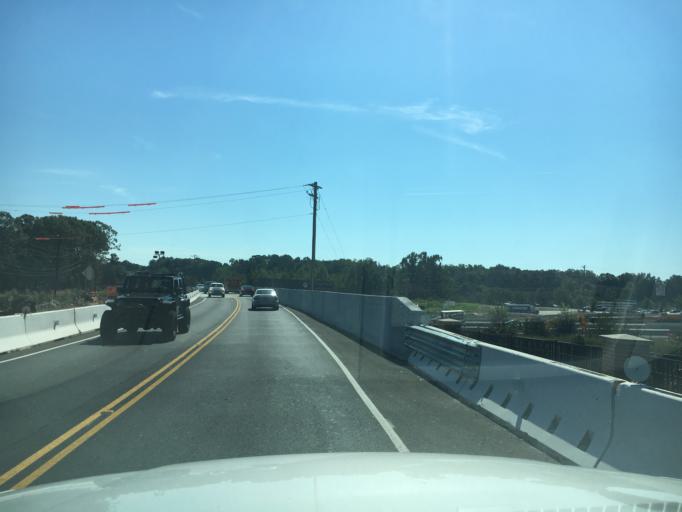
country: US
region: South Carolina
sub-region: Greenville County
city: Mauldin
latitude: 34.8388
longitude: -82.2902
